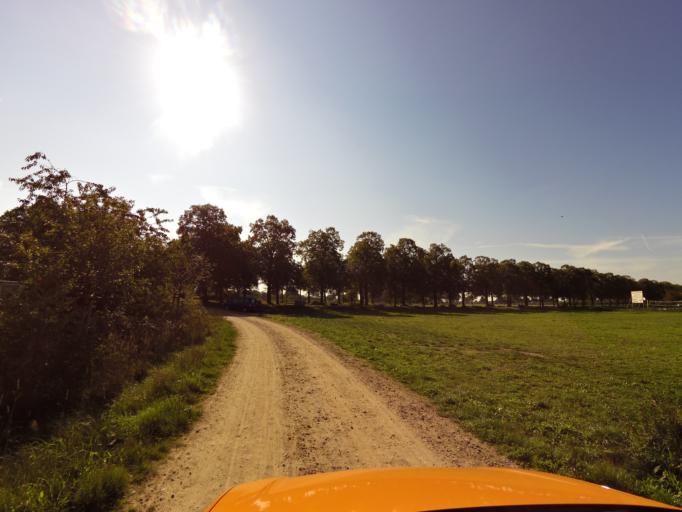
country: DE
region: Brandenburg
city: Grossbeeren
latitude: 52.3531
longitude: 13.2984
